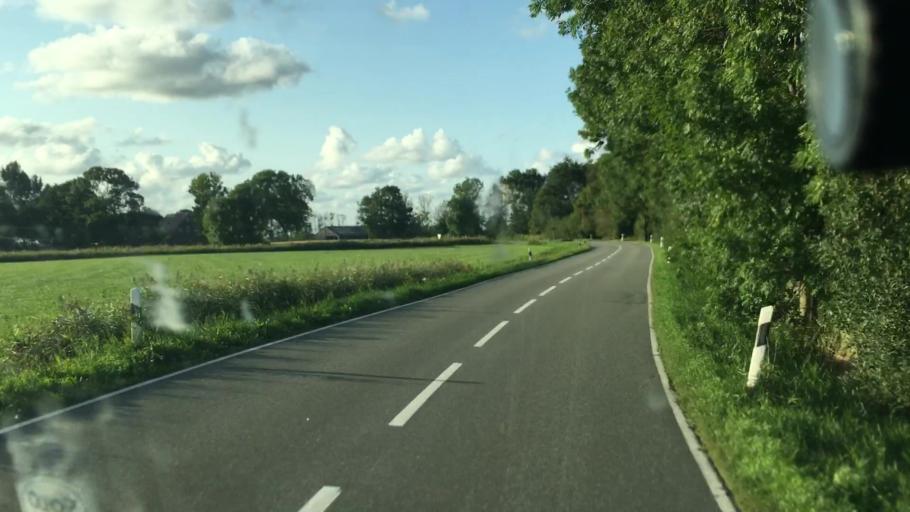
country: DE
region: Lower Saxony
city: Wittmund
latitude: 53.6359
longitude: 7.8292
